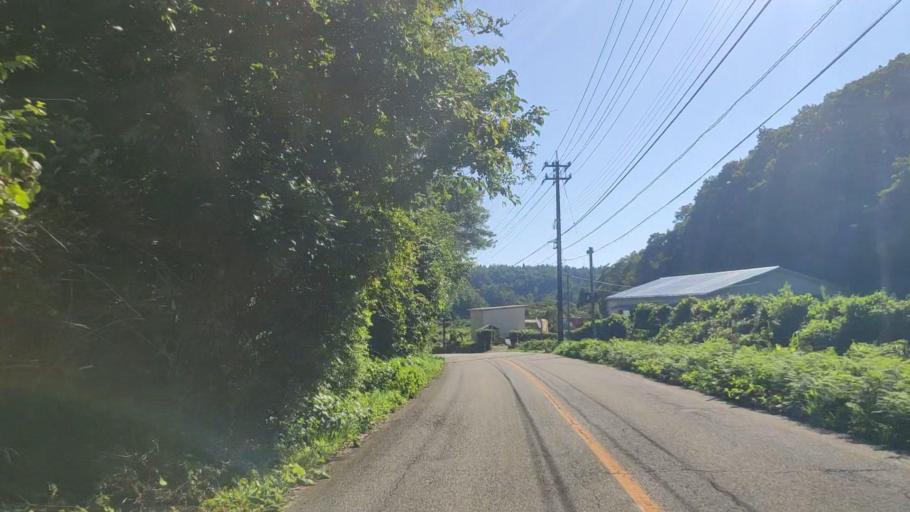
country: JP
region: Ishikawa
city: Nanao
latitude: 37.3188
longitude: 137.1653
